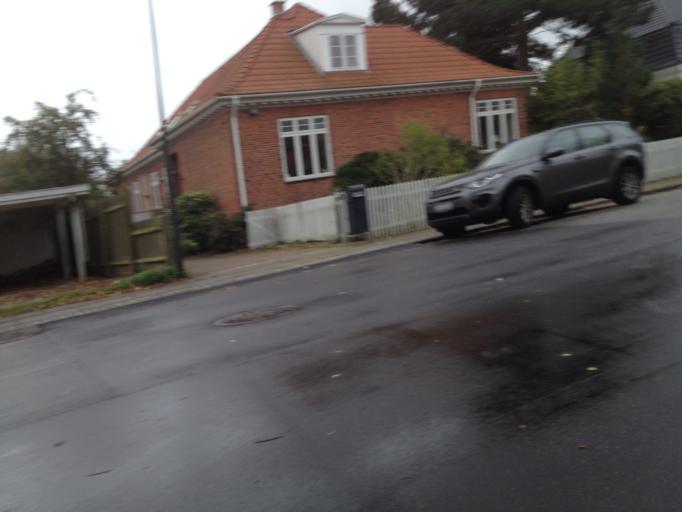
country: DK
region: Capital Region
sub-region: Gentofte Kommune
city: Charlottenlund
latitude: 55.7508
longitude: 12.5648
